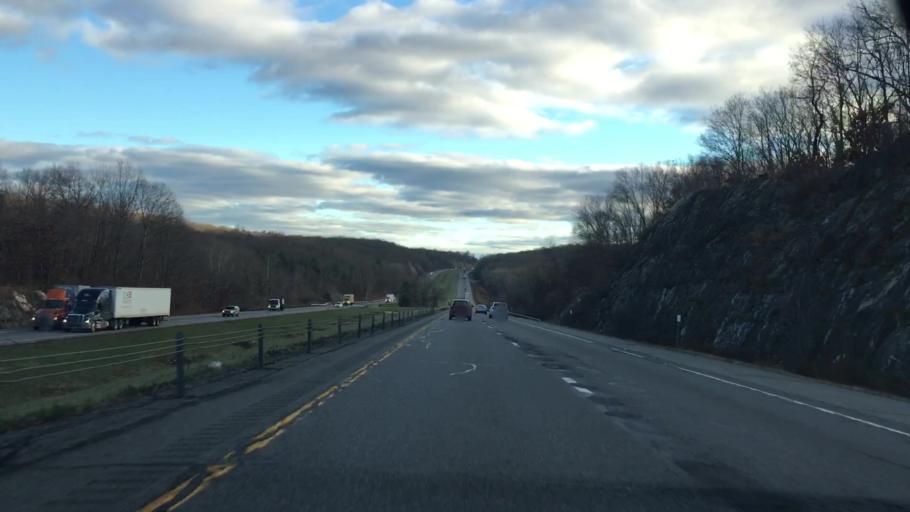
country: US
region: New York
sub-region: Putnam County
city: Lake Carmel
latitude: 41.4538
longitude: -73.6400
